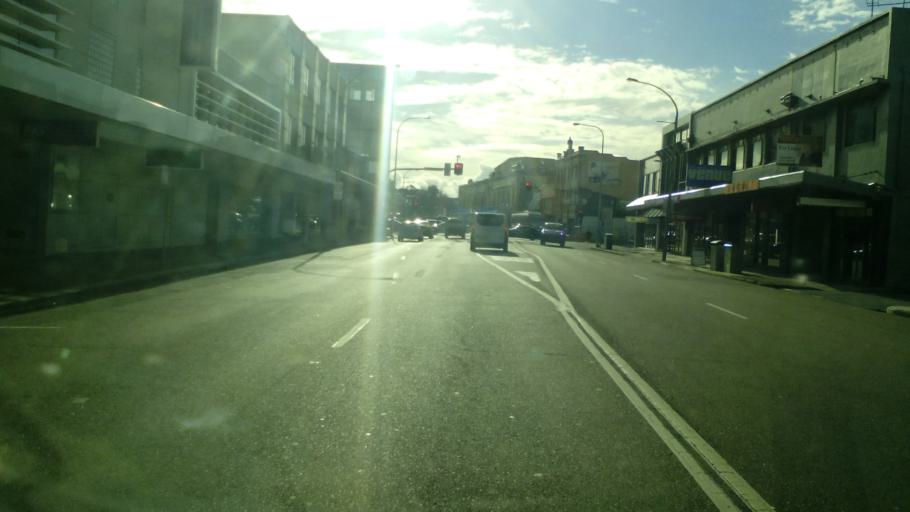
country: AU
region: New South Wales
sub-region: Newcastle
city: Carrington
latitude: -32.9257
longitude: 151.7603
